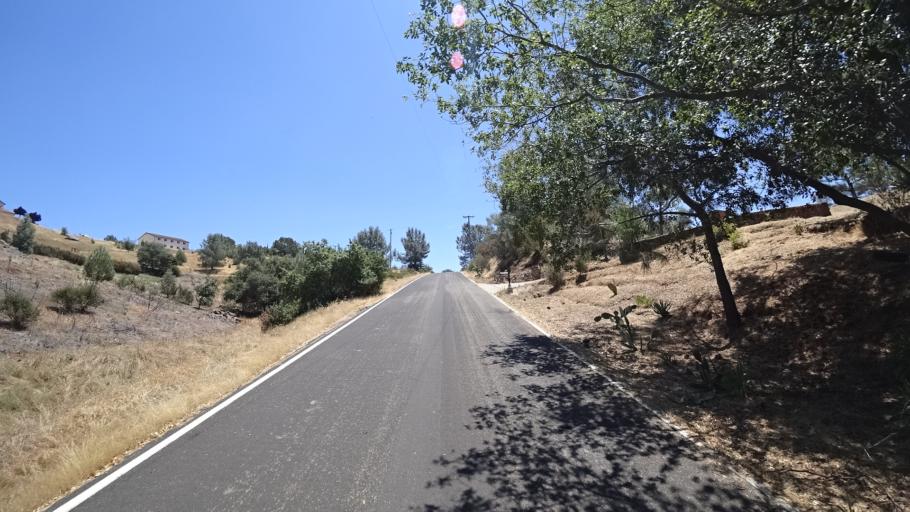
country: US
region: California
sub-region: Calaveras County
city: Rancho Calaveras
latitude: 38.1186
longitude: -120.8458
